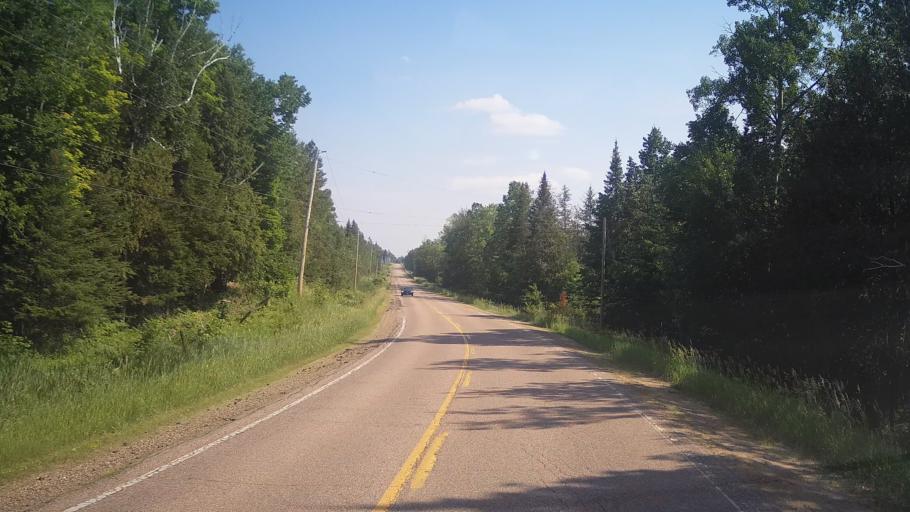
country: CA
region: Ontario
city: Pembroke
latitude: 45.6002
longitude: -77.2328
